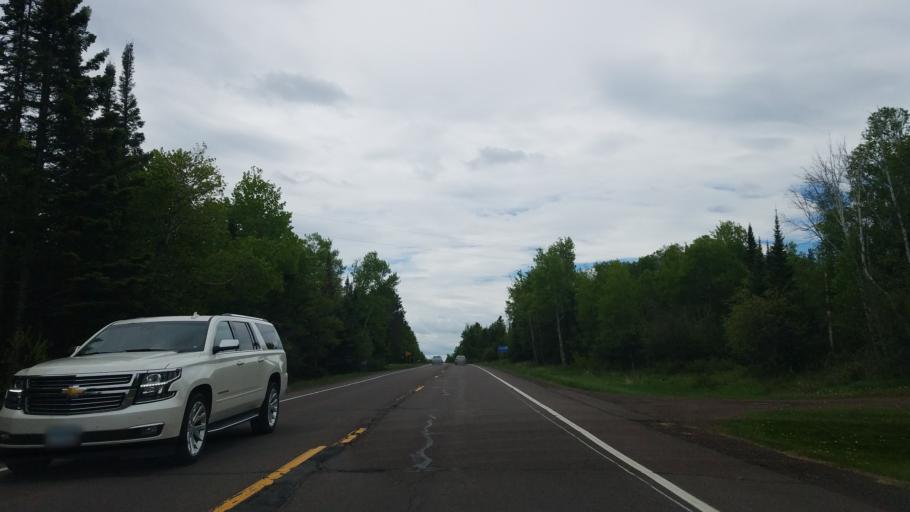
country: US
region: Minnesota
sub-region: Lake County
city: Two Harbors
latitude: 47.0470
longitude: -91.6320
